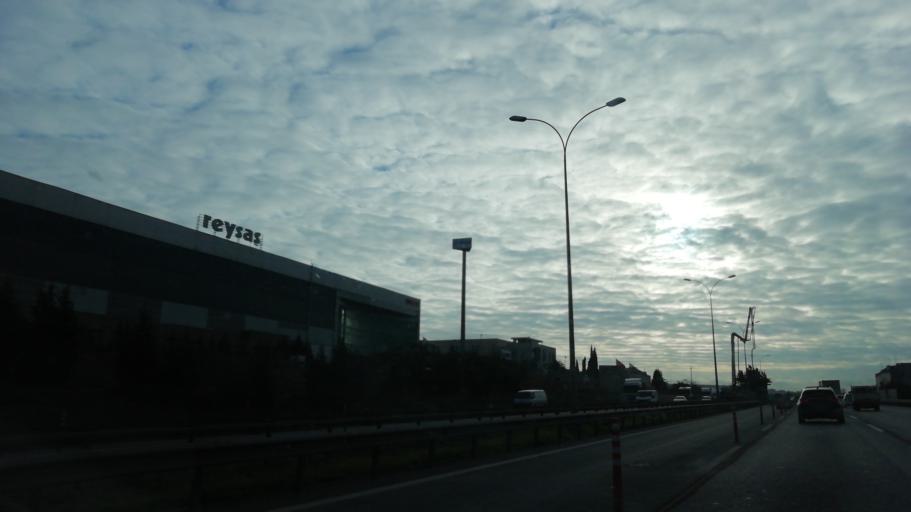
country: TR
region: Kocaeli
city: Balcik
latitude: 40.8840
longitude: 29.3774
